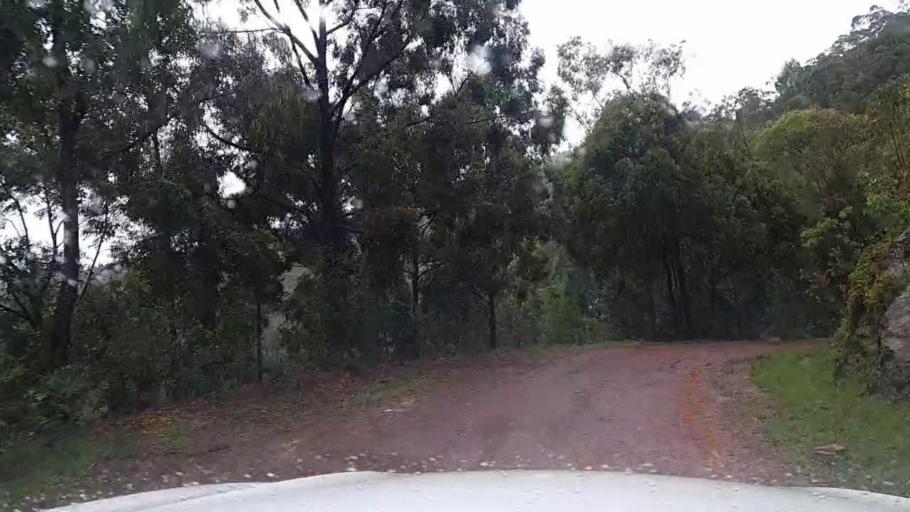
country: RW
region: Kigali
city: Kigali
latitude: -1.7627
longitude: 29.9919
